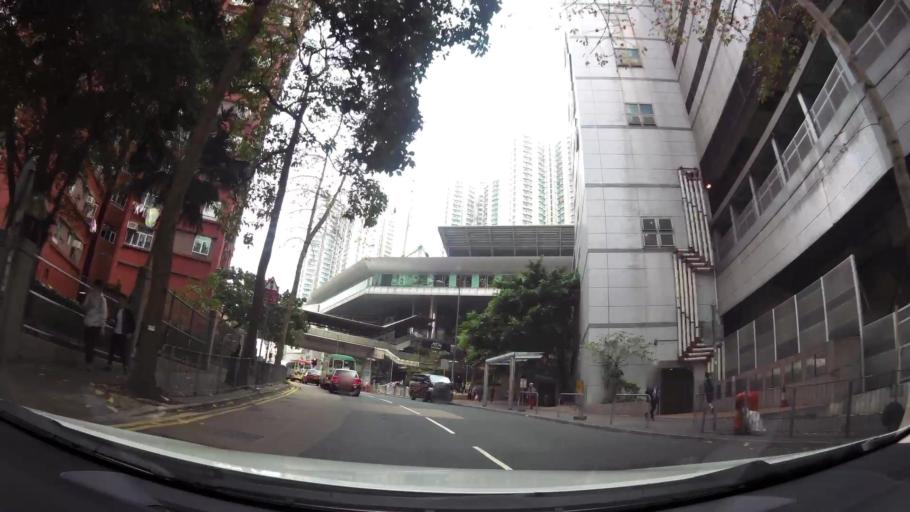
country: HK
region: Kowloon City
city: Kowloon
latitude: 22.3075
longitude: 114.2351
